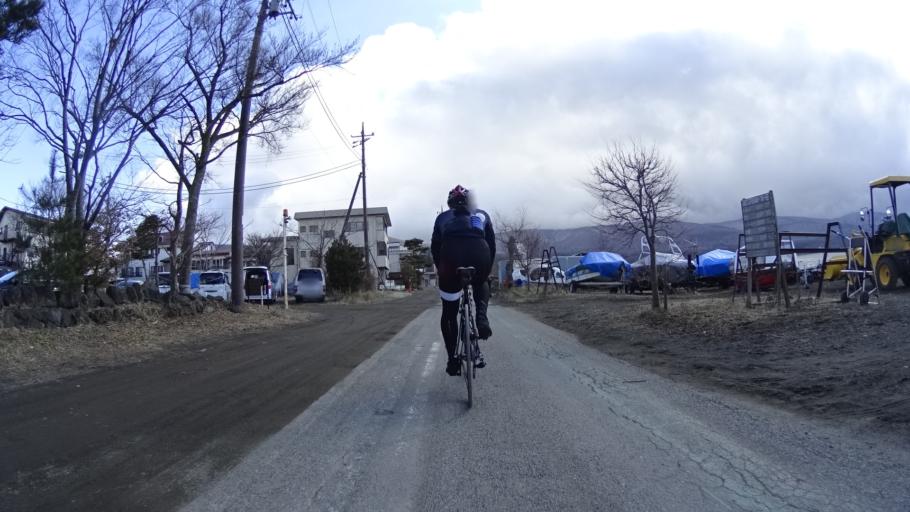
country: JP
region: Shizuoka
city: Gotemba
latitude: 35.4265
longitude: 138.9006
